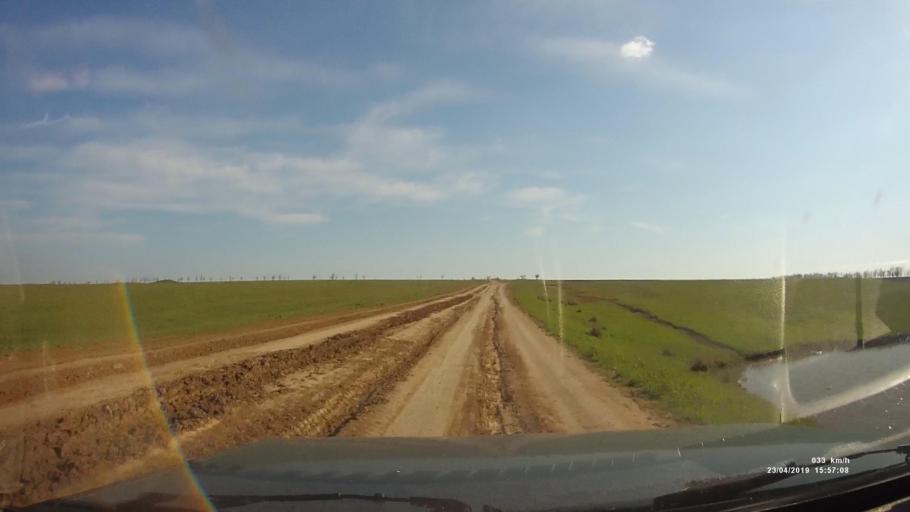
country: RU
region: Rostov
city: Remontnoye
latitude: 46.5334
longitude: 43.1104
